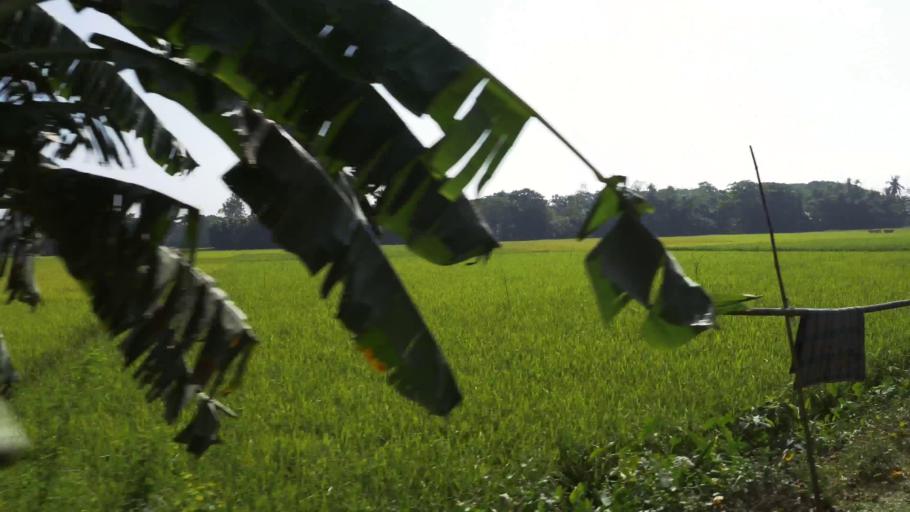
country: BD
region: Dhaka
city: Gafargaon
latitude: 24.5820
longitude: 90.5081
